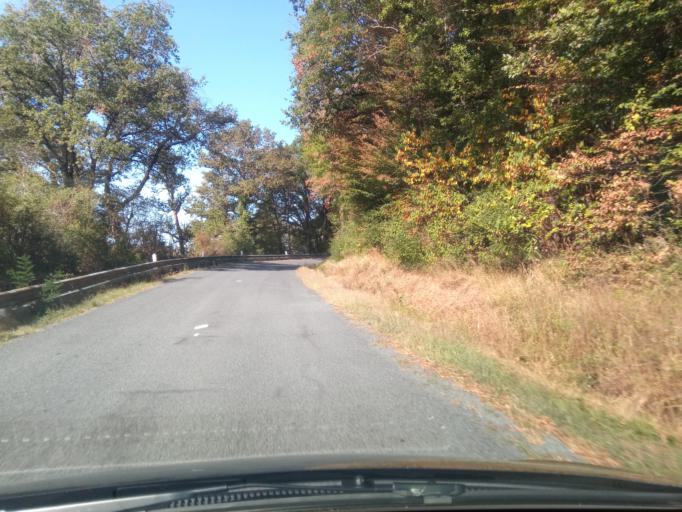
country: FR
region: Poitou-Charentes
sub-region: Departement de la Vienne
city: Saulge
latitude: 46.3447
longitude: 0.8709
